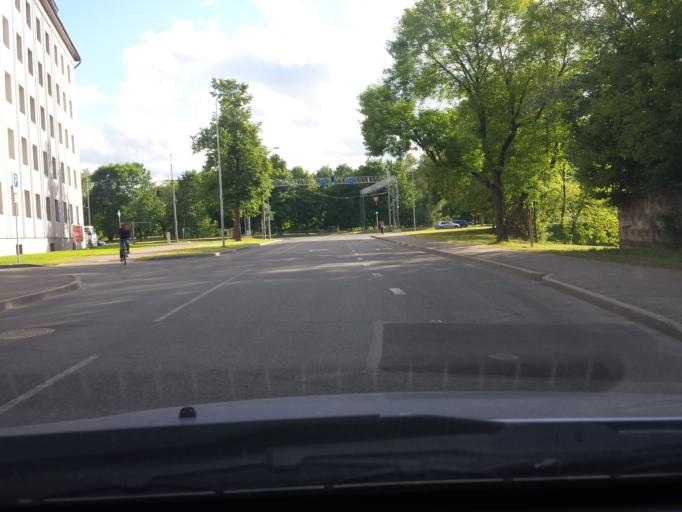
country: LV
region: Riga
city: Riga
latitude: 56.9430
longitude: 24.0887
